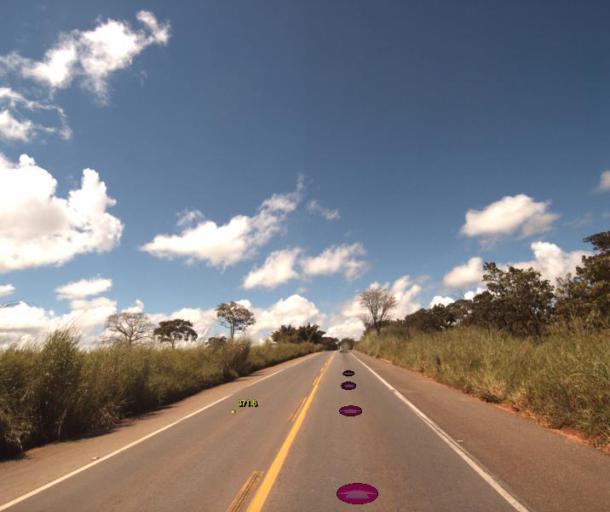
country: BR
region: Goias
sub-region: Jaragua
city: Jaragua
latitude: -15.8343
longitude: -49.2765
